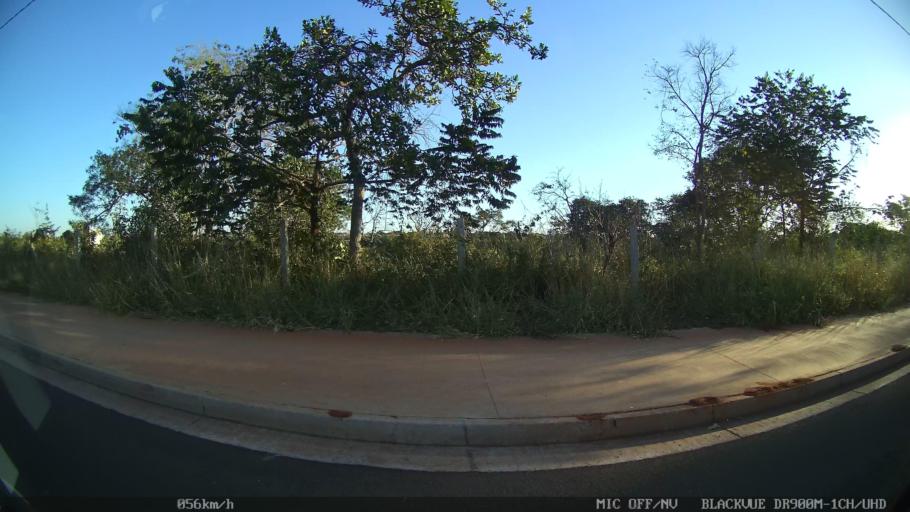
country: BR
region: Sao Paulo
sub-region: Sao Jose Do Rio Preto
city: Sao Jose do Rio Preto
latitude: -20.7691
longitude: -49.3545
